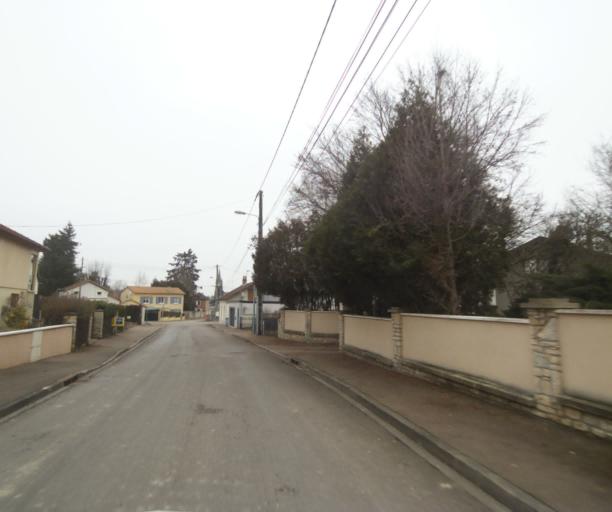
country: FR
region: Champagne-Ardenne
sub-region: Departement de la Haute-Marne
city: Bienville
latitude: 48.5818
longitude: 5.0350
